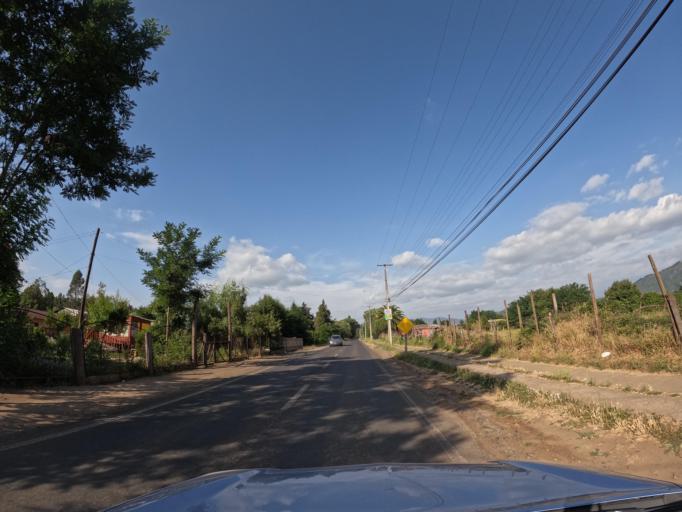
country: CL
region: Maule
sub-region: Provincia de Curico
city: Molina
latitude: -35.2776
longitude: -71.2560
